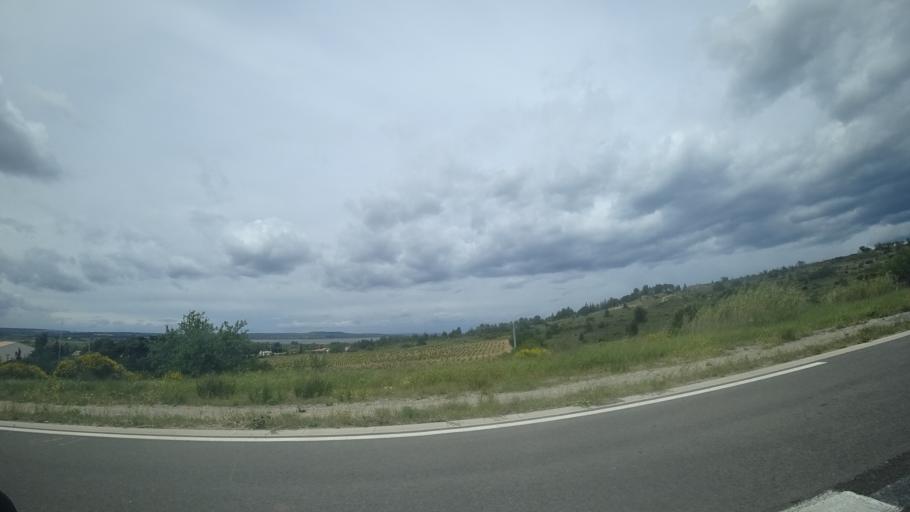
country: FR
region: Languedoc-Roussillon
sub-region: Departement de l'Aude
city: Leucate
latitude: 42.9307
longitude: 3.0141
